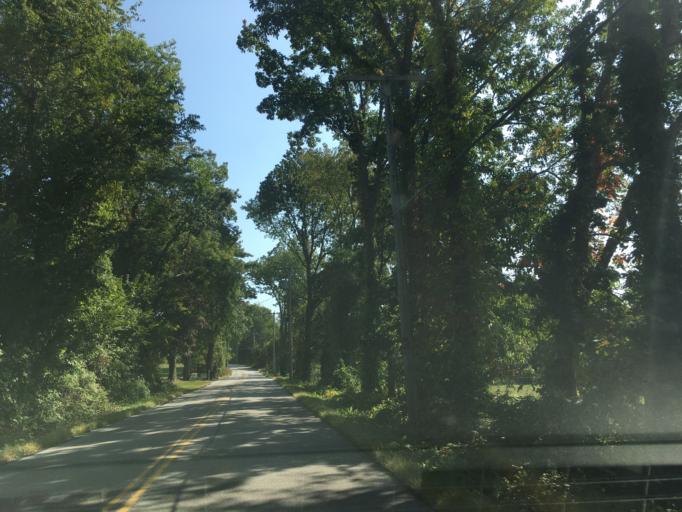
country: US
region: New Hampshire
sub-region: Rockingham County
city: Exeter
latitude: 43.0029
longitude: -70.9077
